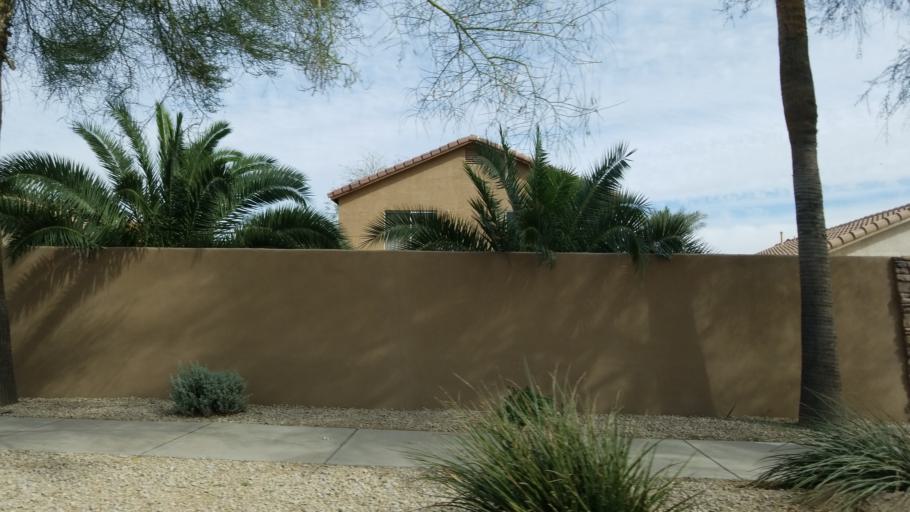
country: US
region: Arizona
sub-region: Maricopa County
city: Glendale
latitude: 33.6755
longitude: -112.0655
